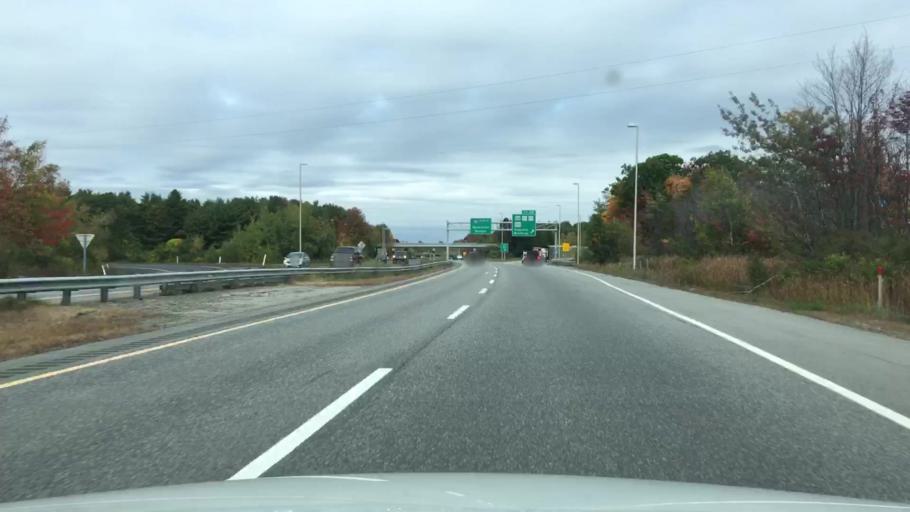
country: US
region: Maine
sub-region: Kennebec County
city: Augusta
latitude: 44.3098
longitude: -69.8083
